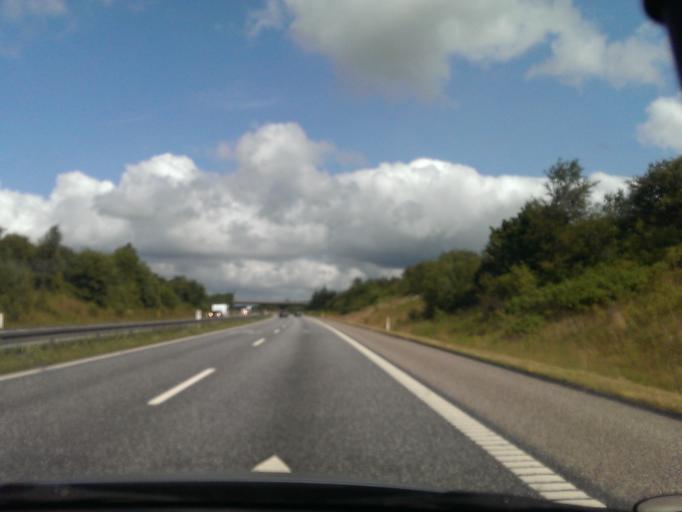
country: DK
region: North Denmark
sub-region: Mariagerfjord Kommune
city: Hobro
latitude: 56.7095
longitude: 9.7287
